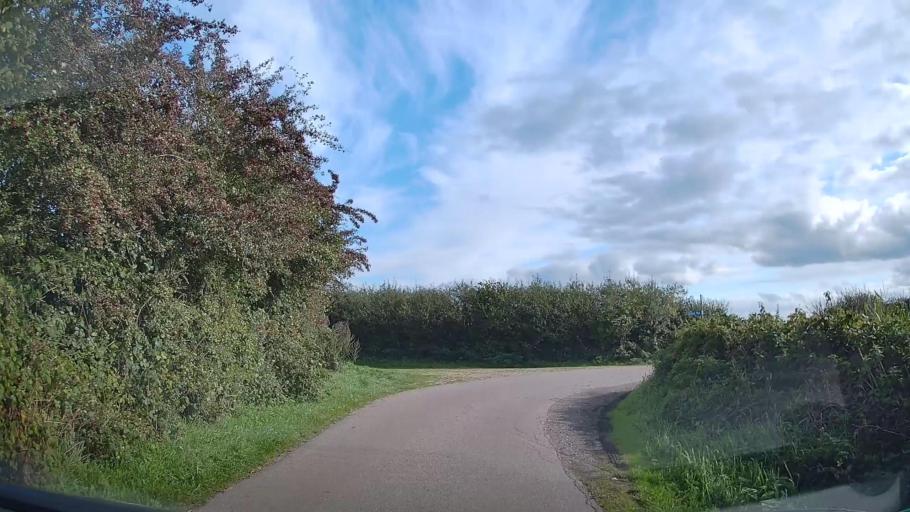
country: DE
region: Schleswig-Holstein
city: Ringsberg
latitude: 54.8192
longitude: 9.5932
